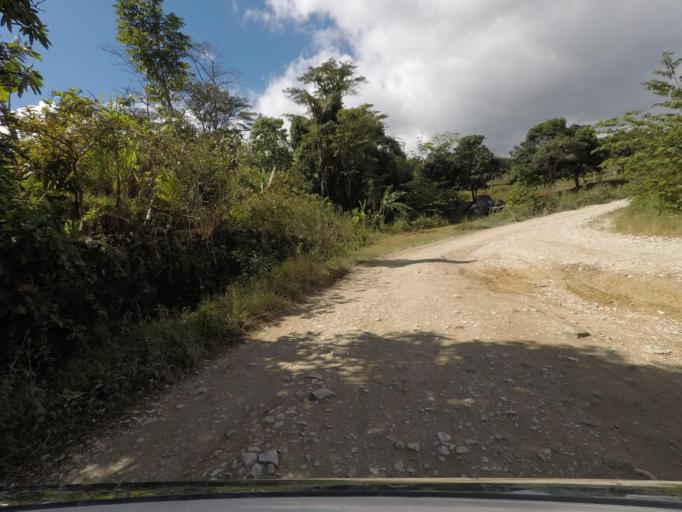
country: TL
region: Baucau
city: Venilale
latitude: -8.6782
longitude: 126.3727
